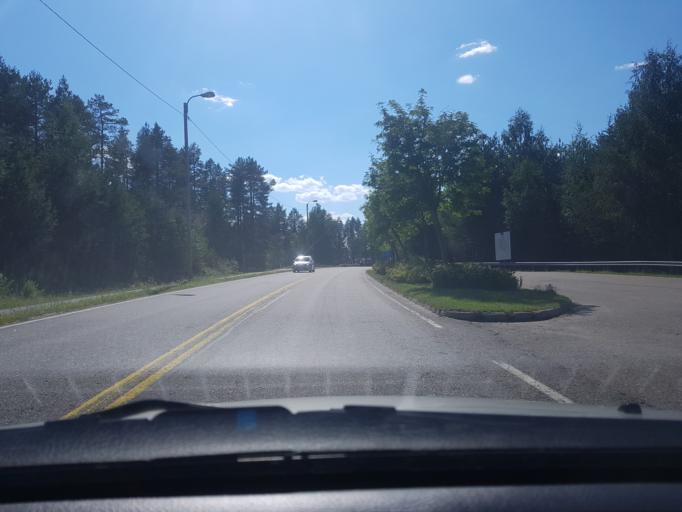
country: FI
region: Kainuu
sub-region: Kehys-Kainuu
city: Kuhmo
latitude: 64.1204
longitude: 29.5797
